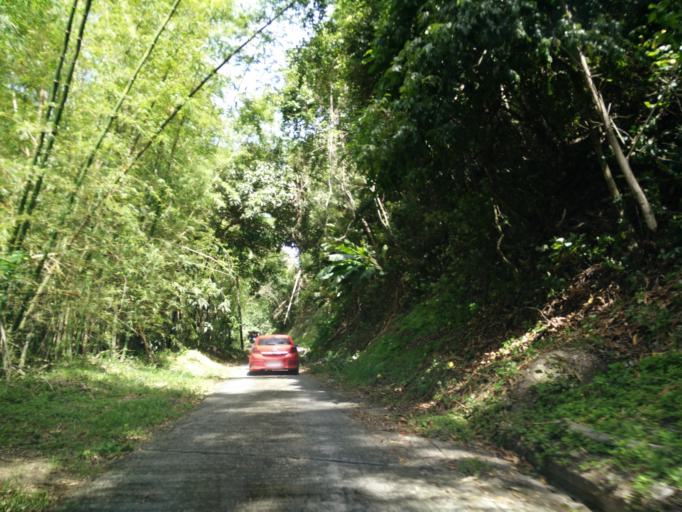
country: MQ
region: Martinique
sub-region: Martinique
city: Saint-Pierre
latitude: 14.7192
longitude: -61.1570
